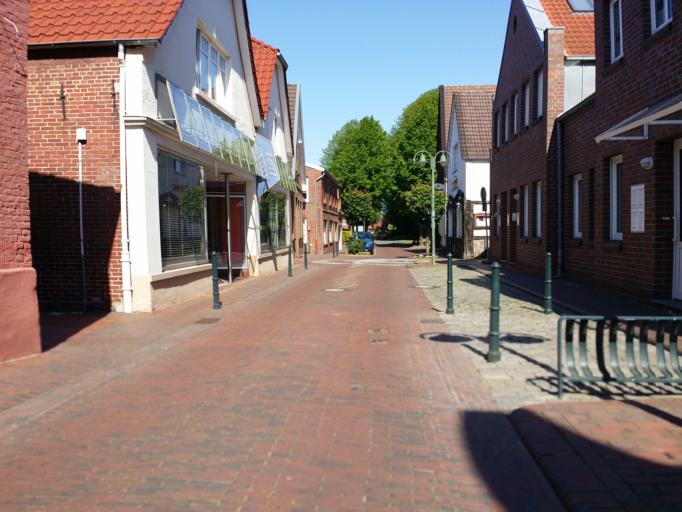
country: DE
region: Lower Saxony
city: Esens
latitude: 53.6471
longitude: 7.6142
